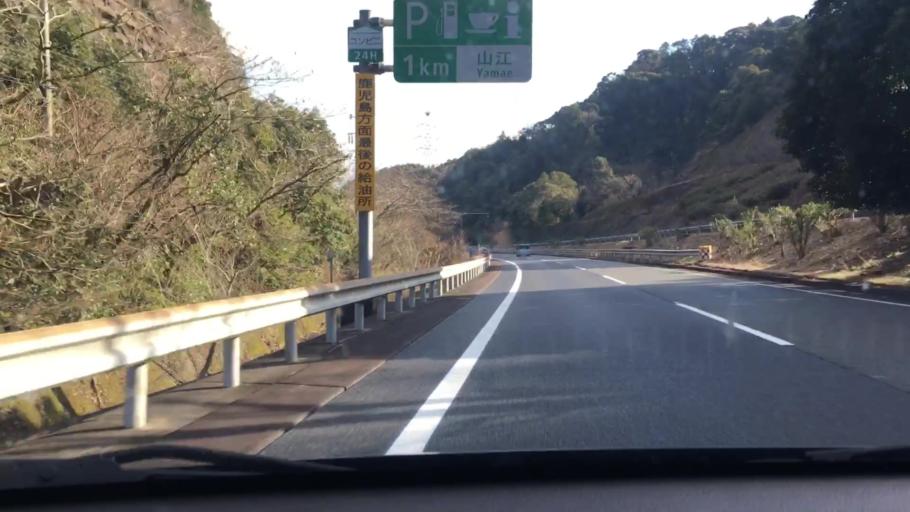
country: JP
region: Kumamoto
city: Hitoyoshi
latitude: 32.2695
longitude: 130.7607
